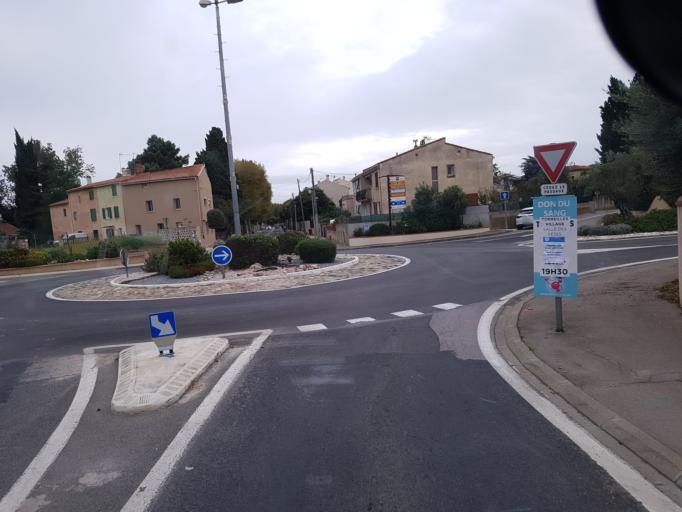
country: FR
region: Languedoc-Roussillon
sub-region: Departement des Pyrenees-Orientales
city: Torreilles
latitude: 42.7596
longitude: 2.9903
